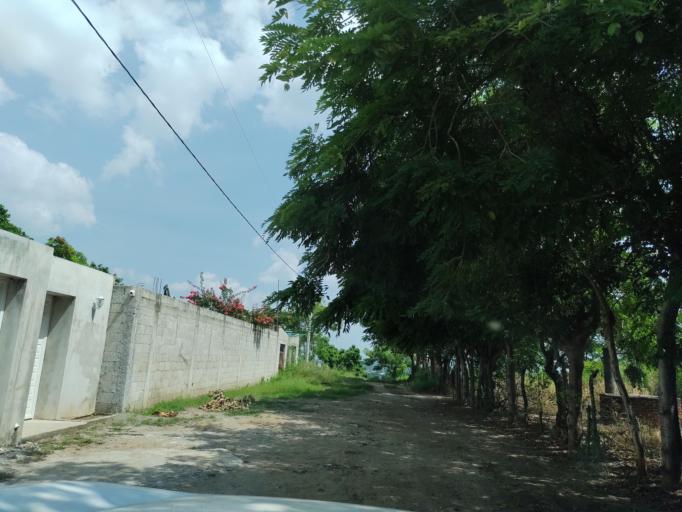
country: MX
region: Veracruz
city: Martinez de la Torre
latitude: 20.0767
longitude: -97.0453
